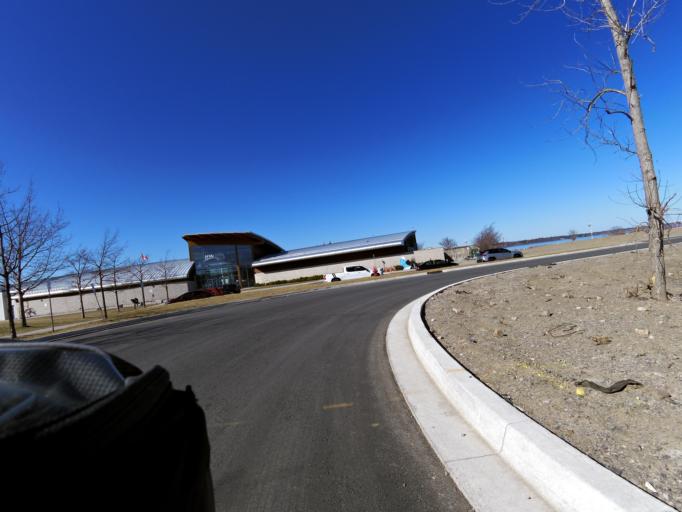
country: CA
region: Ontario
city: Hamilton
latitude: 43.2771
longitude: -79.8606
